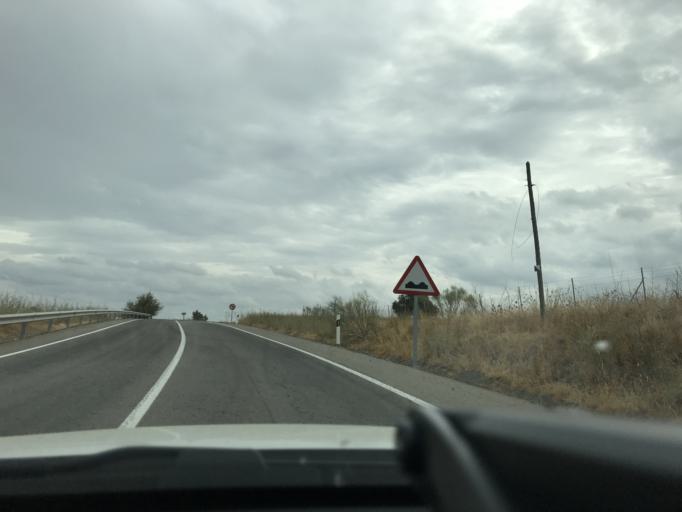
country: ES
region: Andalusia
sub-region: Provincia de Sevilla
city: Cantillana
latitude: 37.6211
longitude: -5.7920
